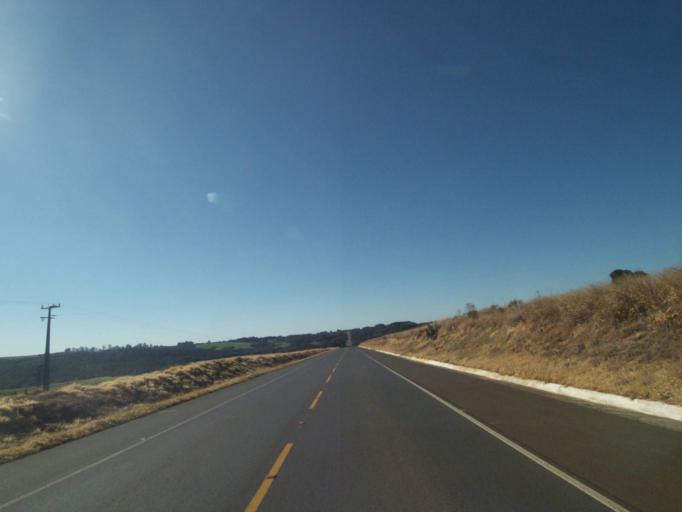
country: BR
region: Parana
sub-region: Tibagi
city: Tibagi
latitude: -24.6210
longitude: -50.4502
